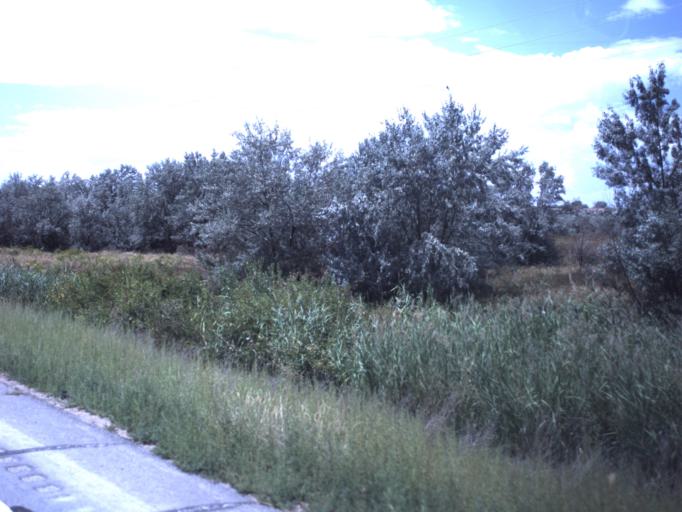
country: US
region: Utah
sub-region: Duchesne County
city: Roosevelt
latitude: 40.1641
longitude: -110.1566
